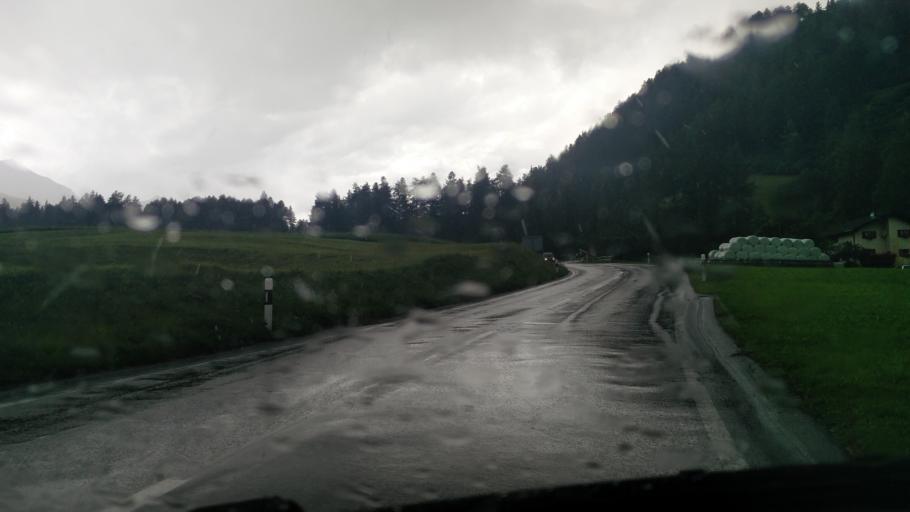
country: IT
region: Trentino-Alto Adige
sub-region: Bolzano
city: Tubre
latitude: 46.6012
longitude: 10.4009
